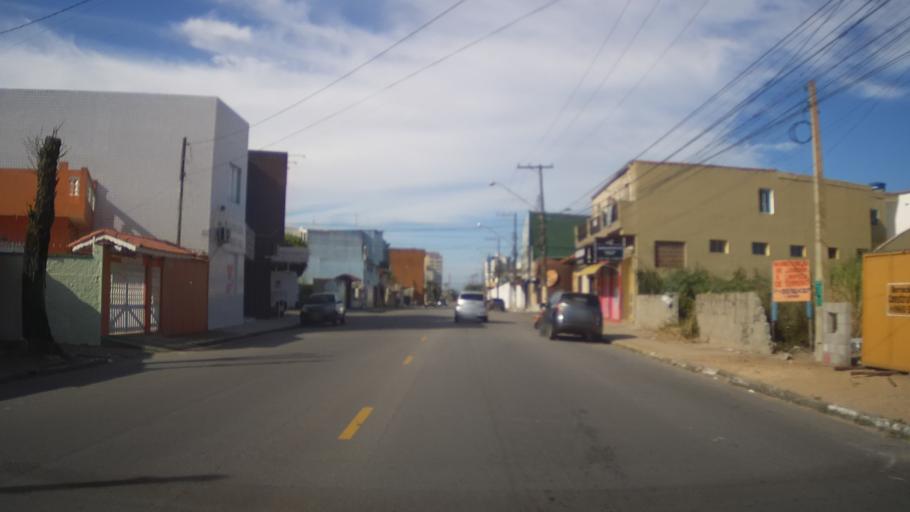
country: BR
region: Sao Paulo
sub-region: Itanhaem
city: Itanhaem
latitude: -24.1773
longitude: -46.7760
